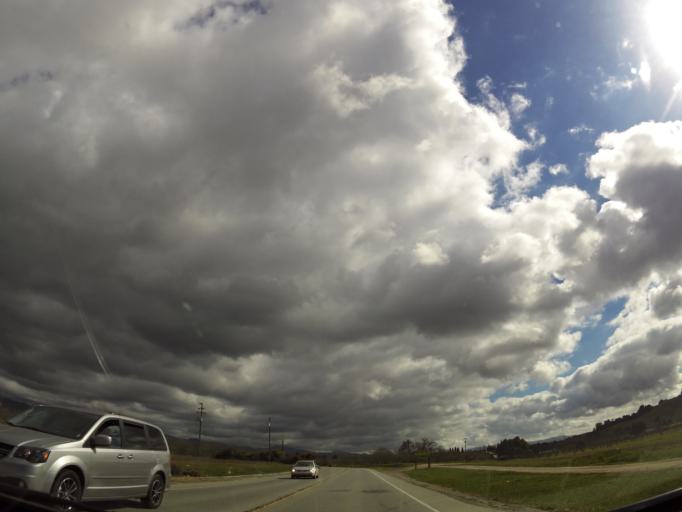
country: US
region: California
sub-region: San Benito County
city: Hollister
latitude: 36.8270
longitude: -121.3925
